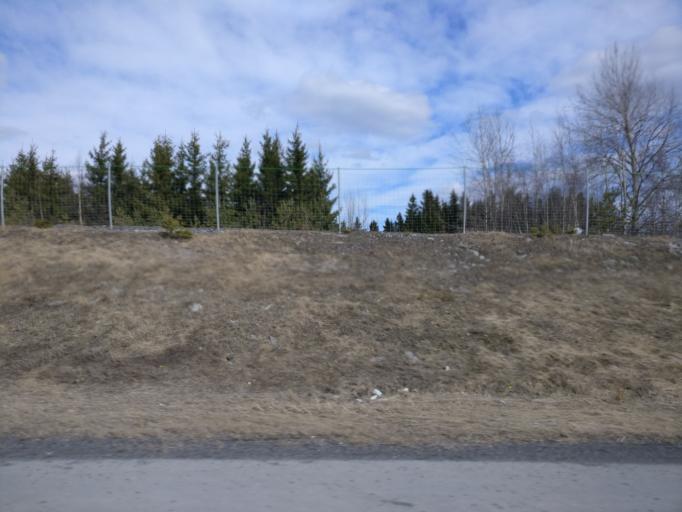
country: FI
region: Pirkanmaa
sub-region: Tampere
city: Lempaeaelae
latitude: 61.3239
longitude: 23.8095
